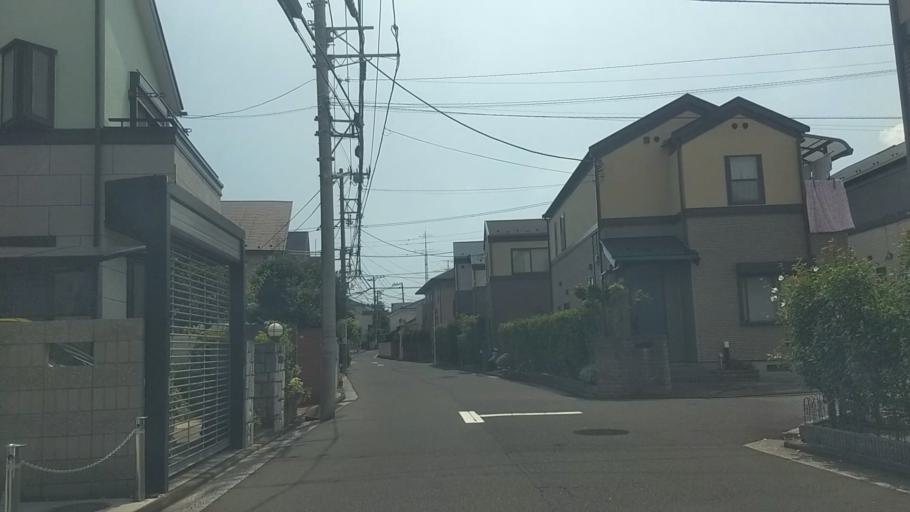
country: JP
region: Kanagawa
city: Yokohama
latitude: 35.5103
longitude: 139.6503
